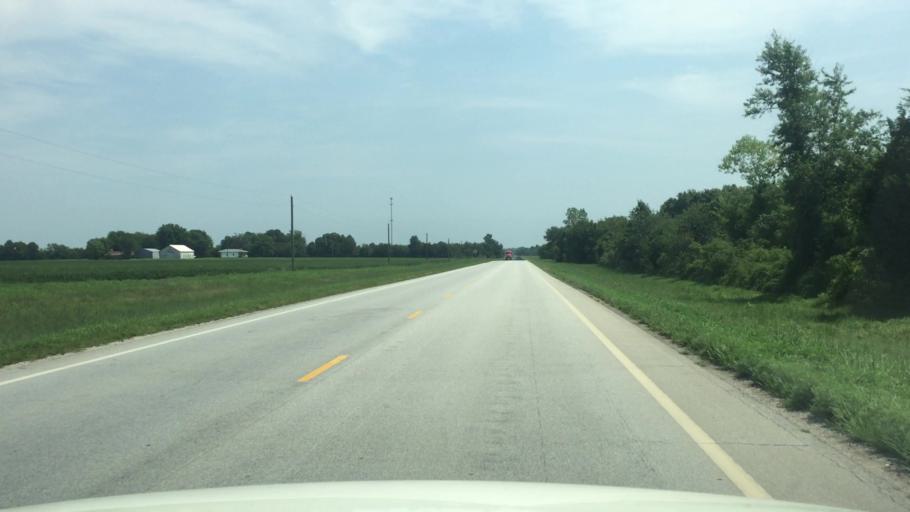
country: US
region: Kansas
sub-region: Cherokee County
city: Columbus
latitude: 37.1787
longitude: -94.8670
